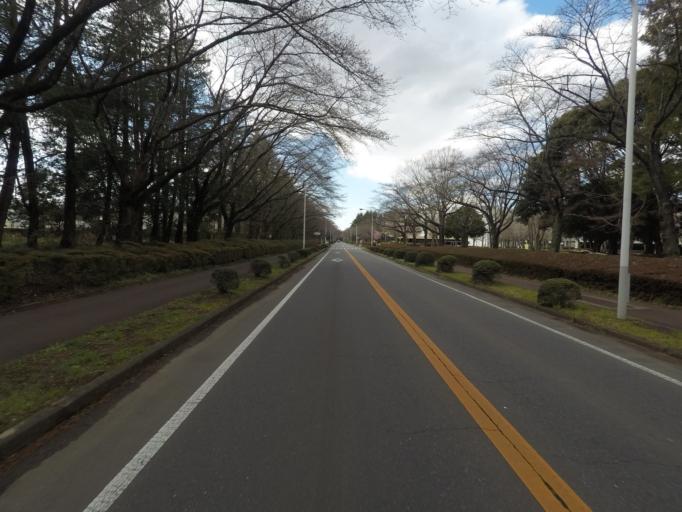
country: JP
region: Ibaraki
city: Naka
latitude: 36.0312
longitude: 140.1027
